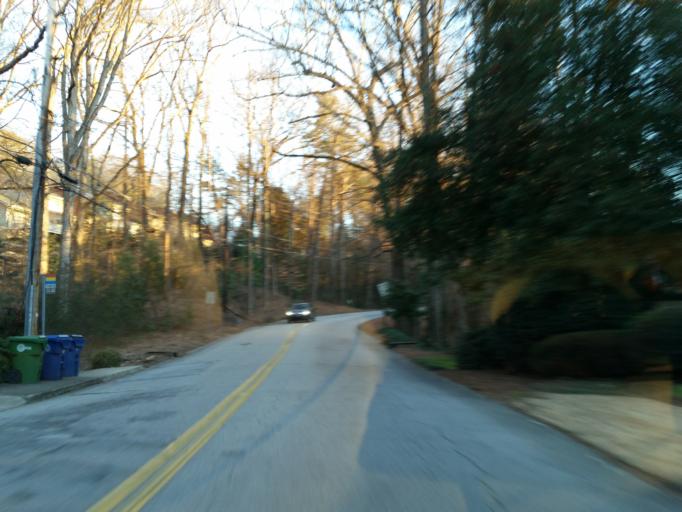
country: US
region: Georgia
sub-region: Cobb County
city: Vinings
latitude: 33.8172
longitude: -84.4319
